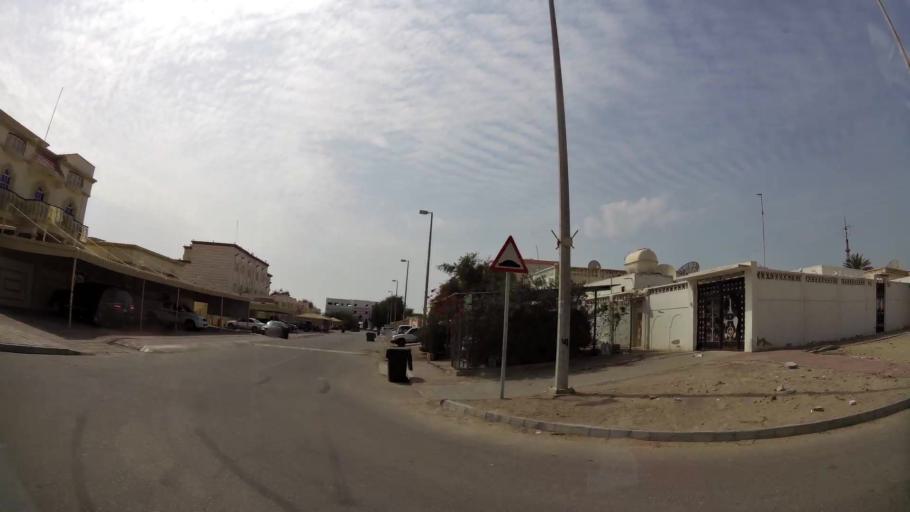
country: AE
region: Abu Dhabi
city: Abu Dhabi
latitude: 24.5518
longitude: 54.6802
